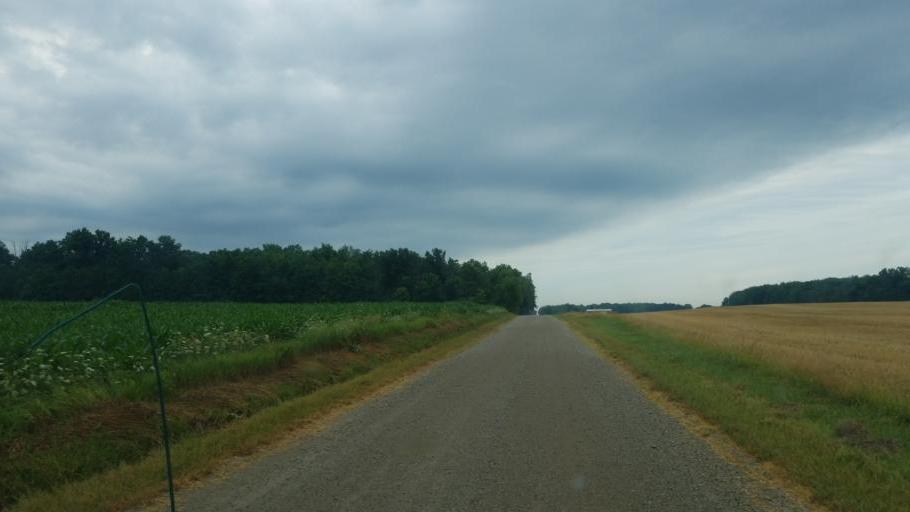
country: US
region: Indiana
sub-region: Steuben County
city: Hamilton
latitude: 41.4933
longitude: -84.9110
